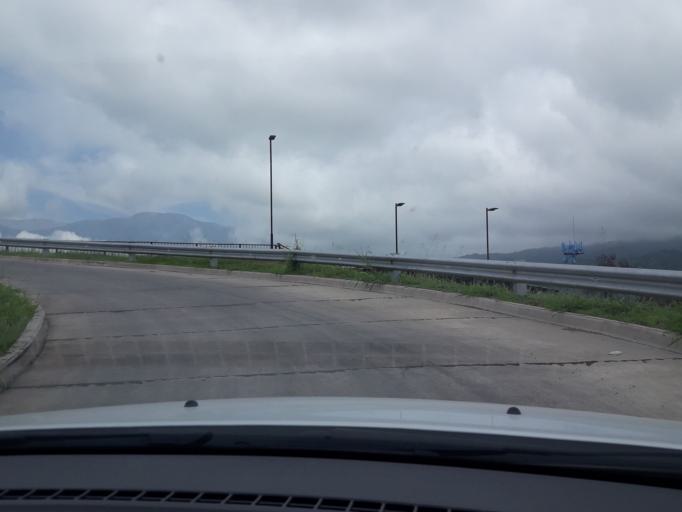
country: AR
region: Jujuy
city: San Salvador de Jujuy
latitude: -24.1807
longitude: -65.3269
